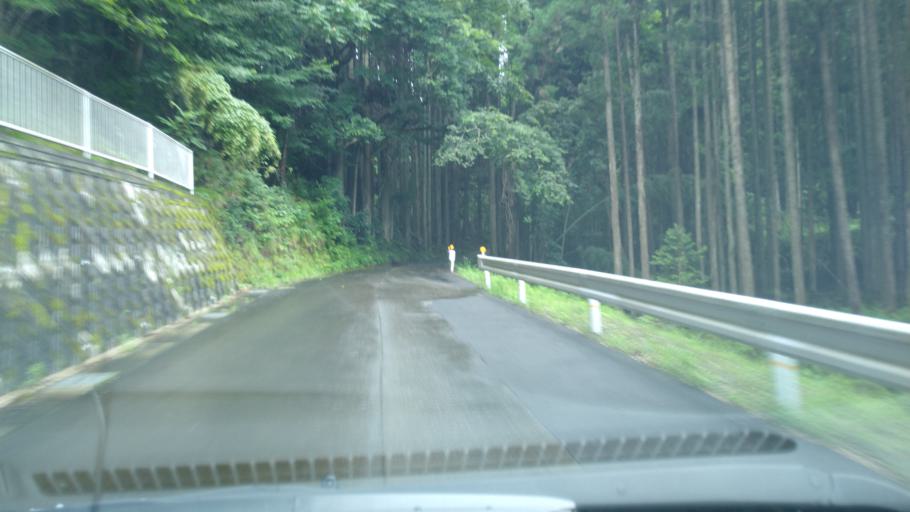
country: JP
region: Kyoto
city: Ayabe
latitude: 35.2288
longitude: 135.2726
